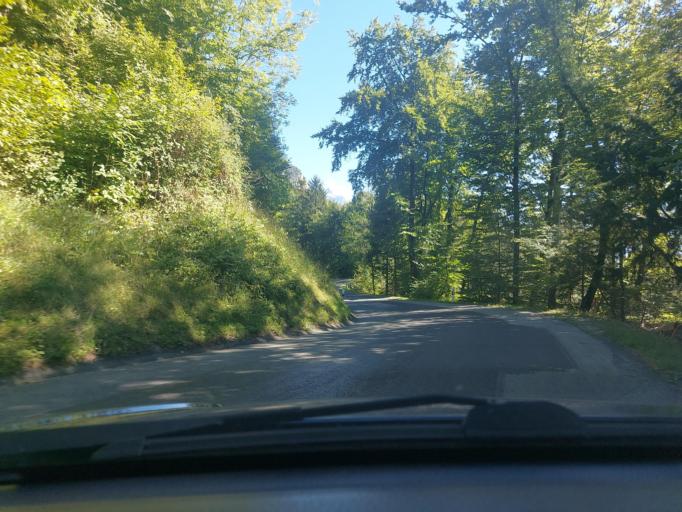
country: CH
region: Vaud
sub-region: Aigle District
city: Aigle
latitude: 46.3403
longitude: 6.9656
